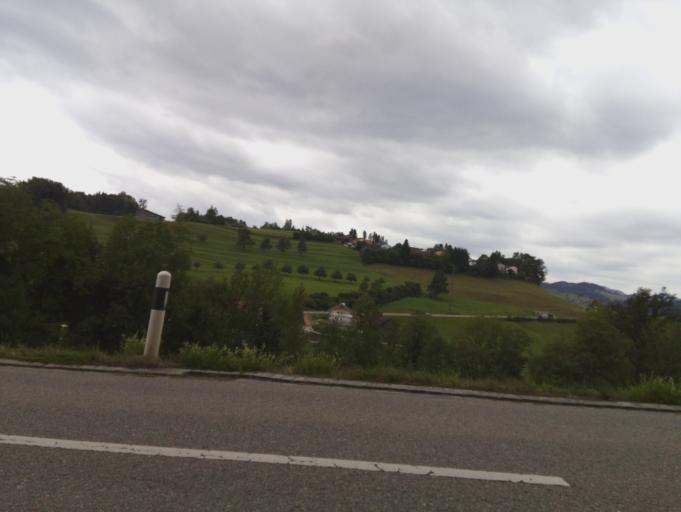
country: CH
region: Saint Gallen
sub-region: Wahlkreis Wil
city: Jonschwil
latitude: 47.4113
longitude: 9.0870
